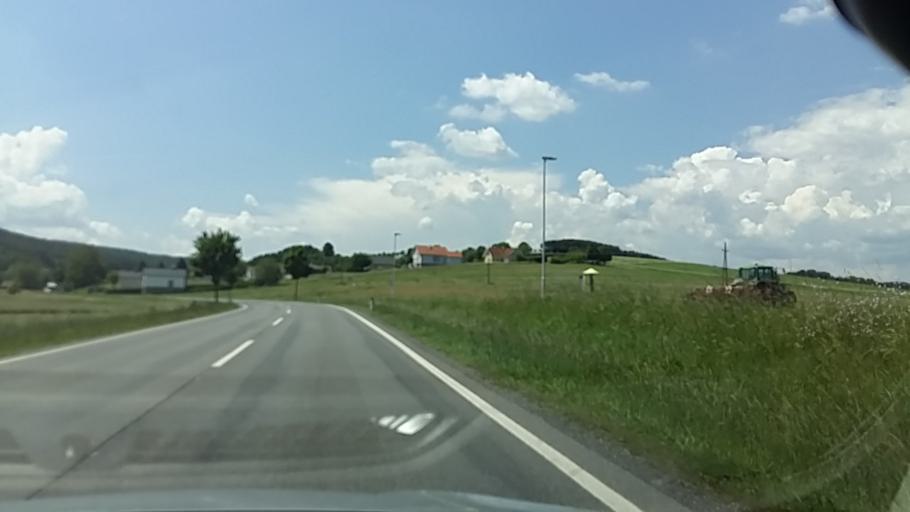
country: AT
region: Burgenland
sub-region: Politischer Bezirk Oberpullendorf
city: Lockenhaus
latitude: 47.4068
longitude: 16.3793
